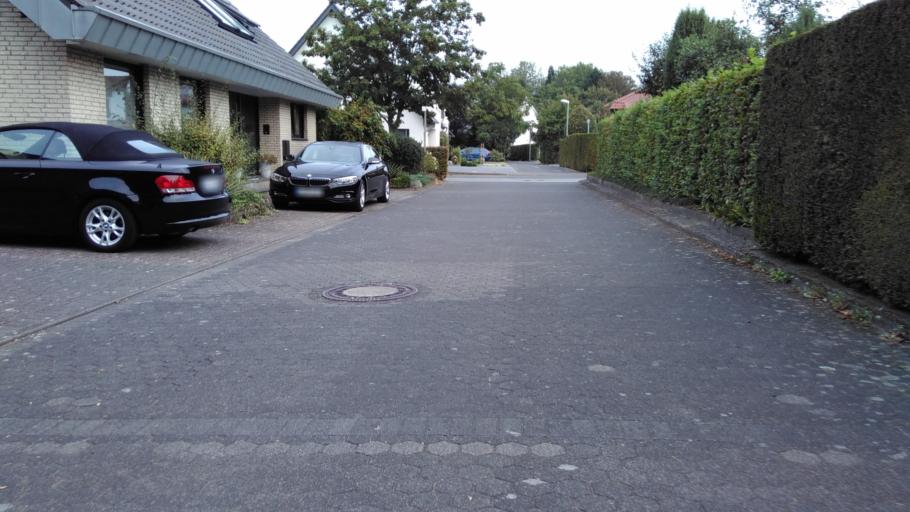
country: DE
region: North Rhine-Westphalia
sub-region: Regierungsbezirk Detmold
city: Verl
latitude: 51.8760
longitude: 8.4963
